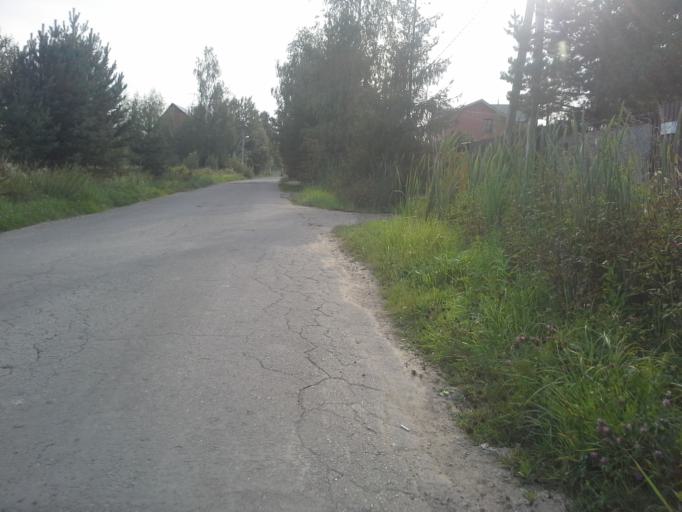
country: RU
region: Moskovskaya
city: Aprelevka
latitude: 55.5584
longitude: 37.0606
